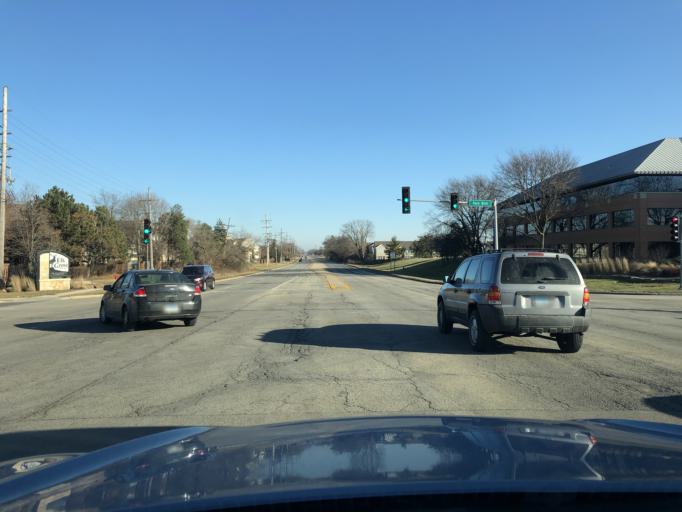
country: US
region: Illinois
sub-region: DuPage County
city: Itasca
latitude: 41.9924
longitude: -88.0206
